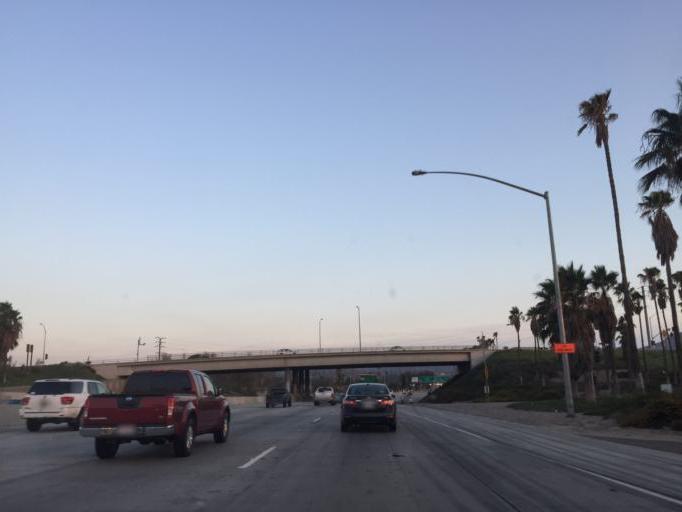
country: US
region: California
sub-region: San Bernardino County
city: Colton
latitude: 34.0791
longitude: -117.2973
